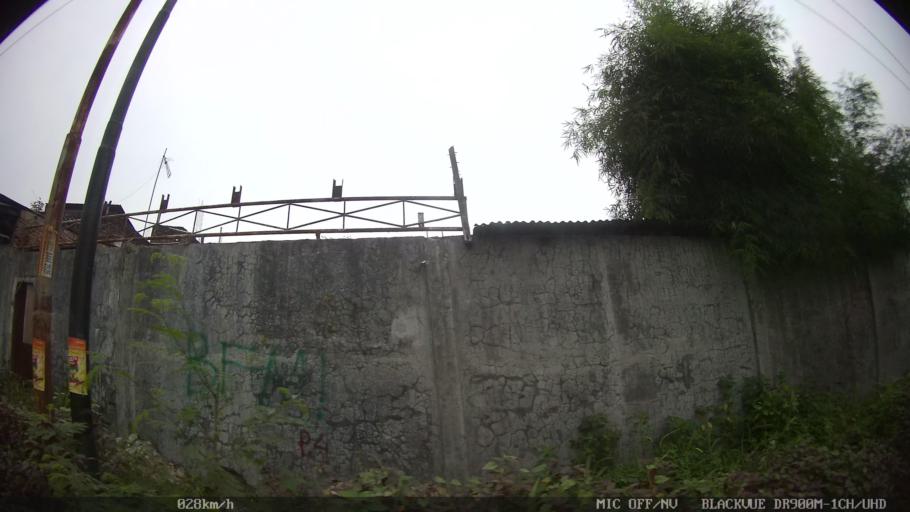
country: ID
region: North Sumatra
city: Deli Tua
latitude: 3.5486
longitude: 98.7138
